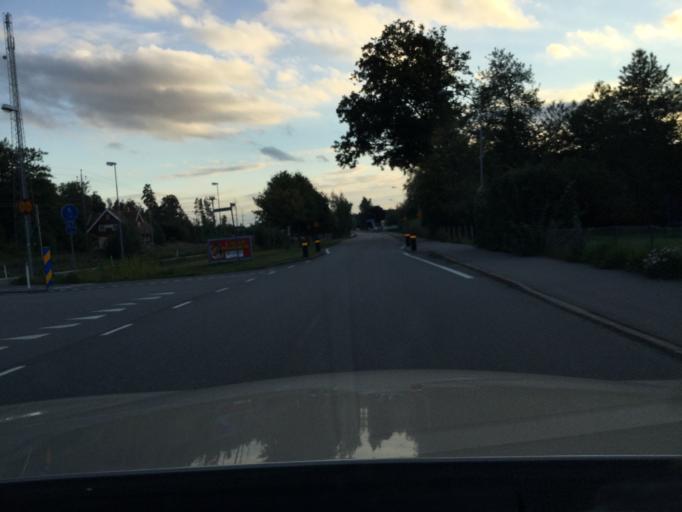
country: SE
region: Kronoberg
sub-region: Almhults Kommun
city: AElmhult
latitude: 56.6354
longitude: 14.2179
